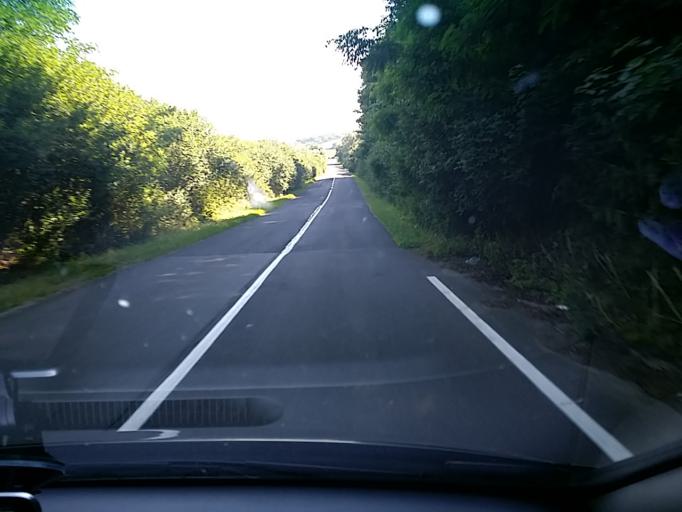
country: HU
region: Nograd
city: Karancskeszi
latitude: 48.2211
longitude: 19.6062
